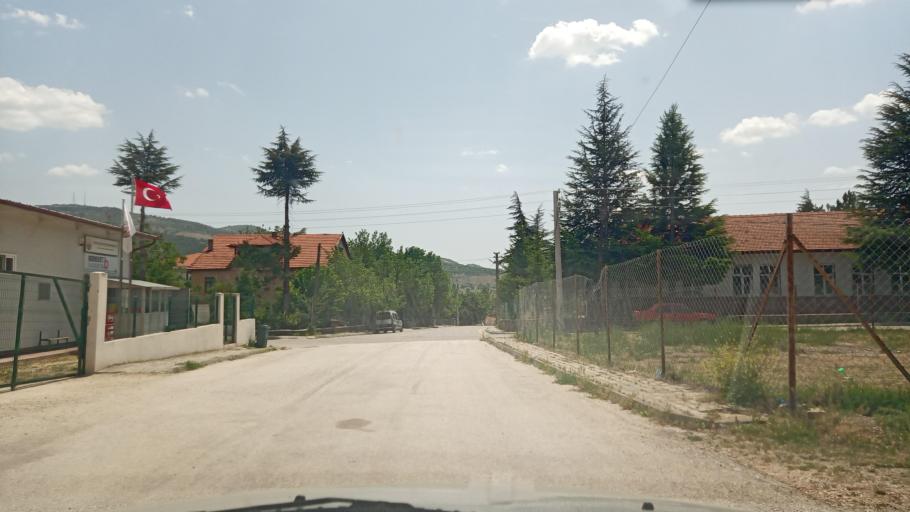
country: TR
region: Bolu
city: Seben
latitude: 40.4125
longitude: 31.5729
